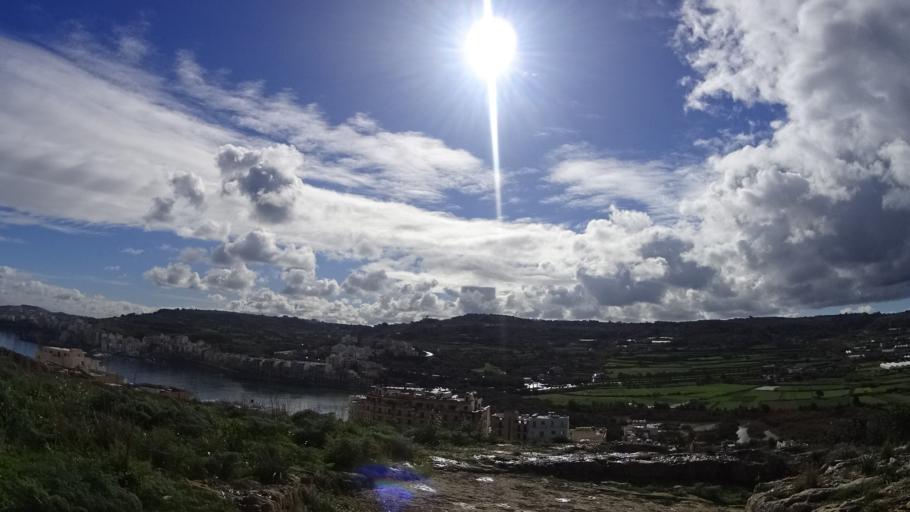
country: MT
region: Il-Mellieha
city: Mellieha
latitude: 35.9487
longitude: 14.3808
